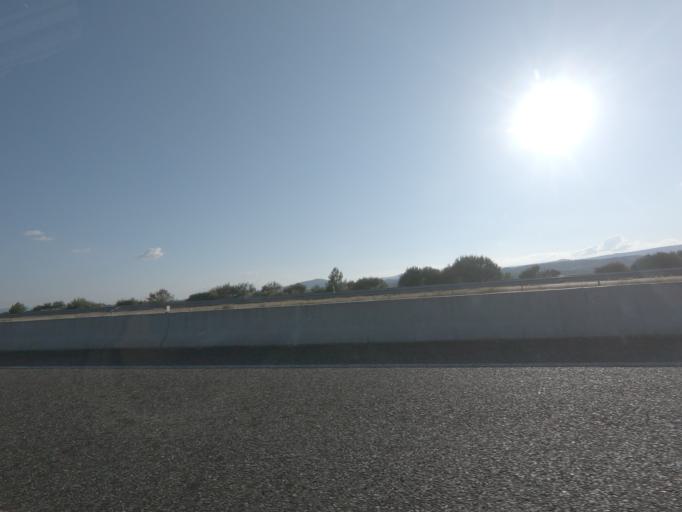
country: ES
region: Galicia
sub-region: Provincia de Ourense
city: Oimbra
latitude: 41.8305
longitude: -7.4214
